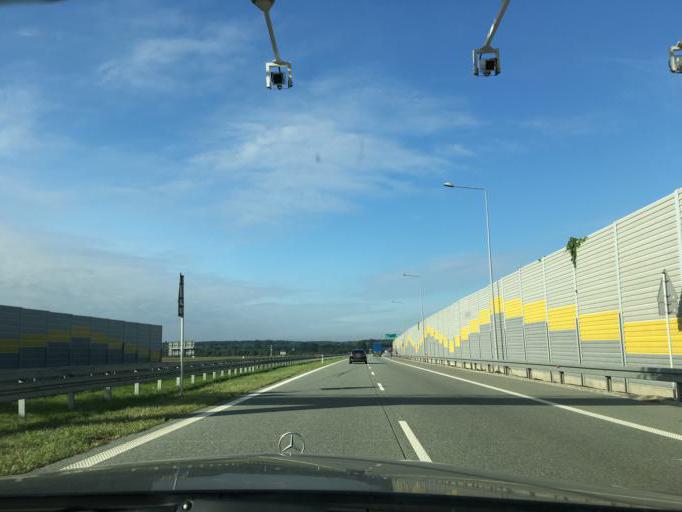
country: PL
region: Lodz Voivodeship
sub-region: Powiat pabianicki
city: Pabianice
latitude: 51.6116
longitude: 19.3580
